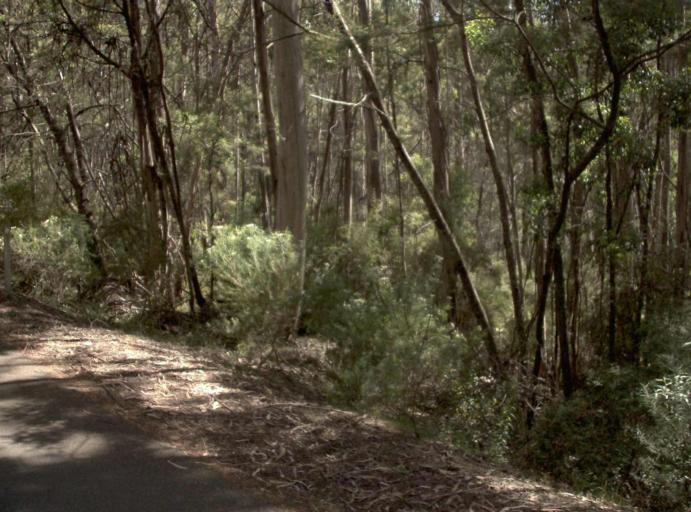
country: AU
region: Victoria
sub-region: East Gippsland
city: Lakes Entrance
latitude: -37.4301
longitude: 148.1274
